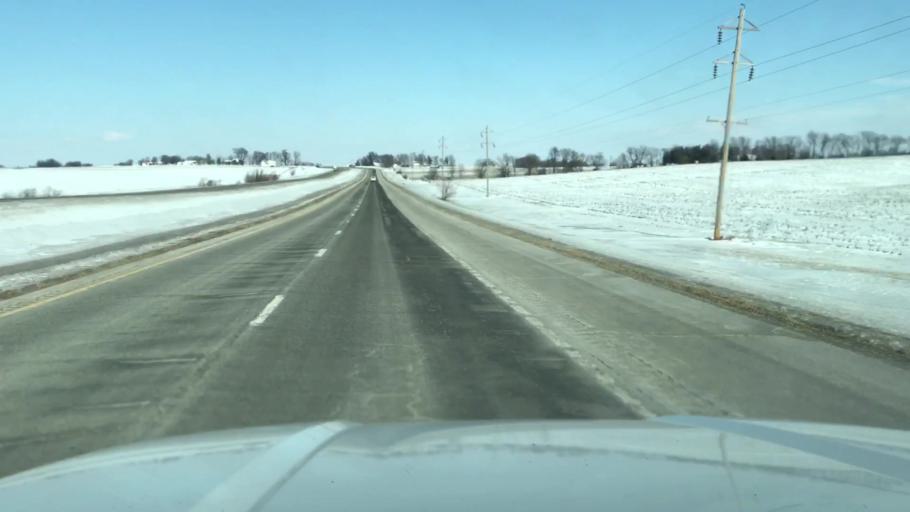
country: US
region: Missouri
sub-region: Nodaway County
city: Maryville
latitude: 40.2618
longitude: -94.8667
